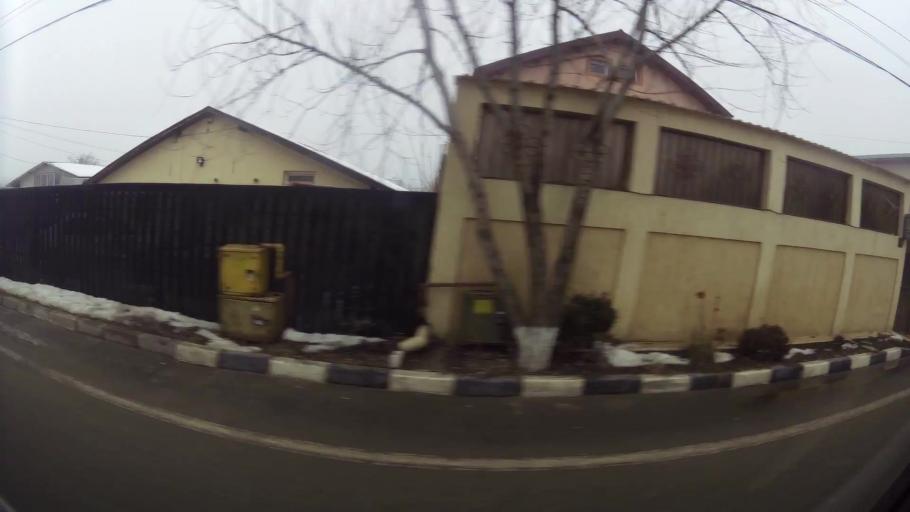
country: RO
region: Ilfov
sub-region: Comuna Chiajna
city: Chiajna
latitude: 44.4554
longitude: 25.9684
